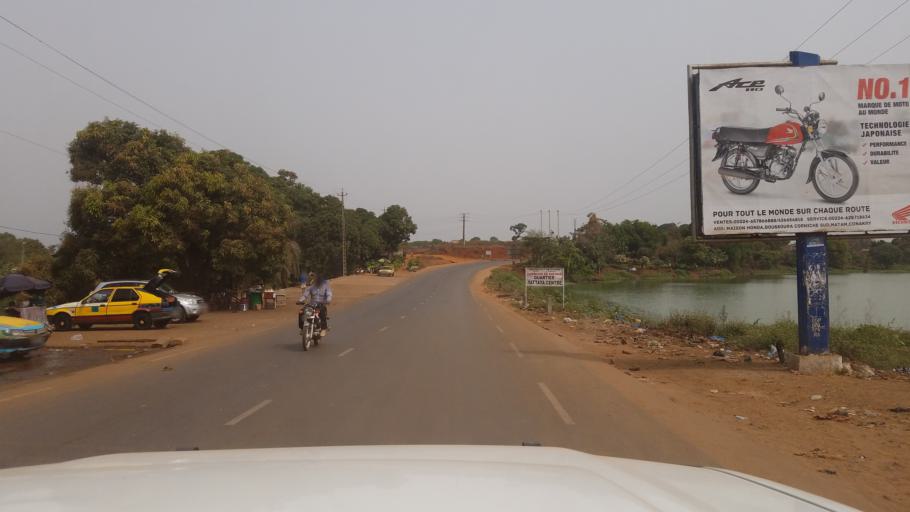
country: GN
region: Kindia
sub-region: Prefecture de Dubreka
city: Dubreka
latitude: 9.6737
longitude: -13.5839
